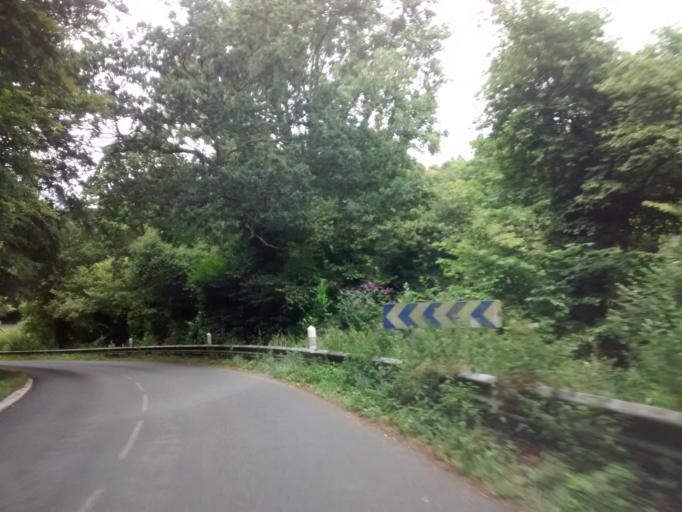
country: FR
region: Brittany
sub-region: Departement des Cotes-d'Armor
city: Trelevern
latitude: 48.7909
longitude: -3.3789
